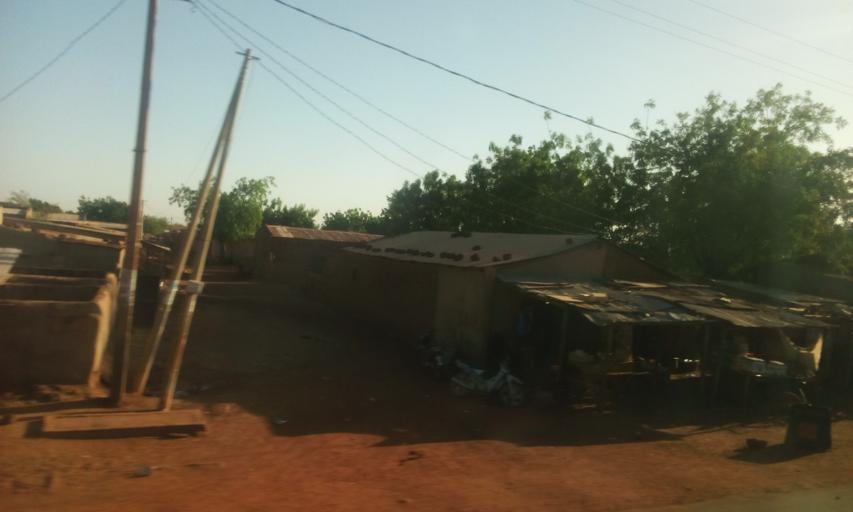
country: ML
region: Segou
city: Baroueli
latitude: 12.7841
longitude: -6.9507
